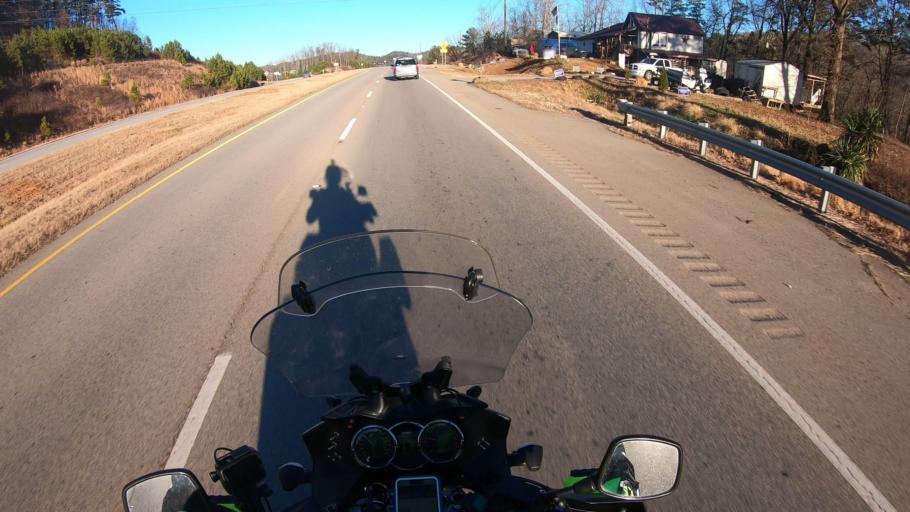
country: US
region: Georgia
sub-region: Bartow County
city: Emerson
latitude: 34.1173
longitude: -84.7713
